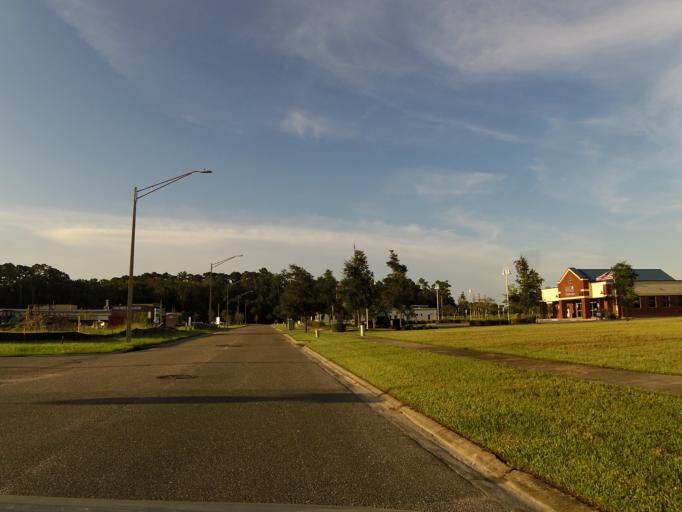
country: US
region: Florida
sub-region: Clay County
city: Orange Park
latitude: 30.2240
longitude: -81.7030
